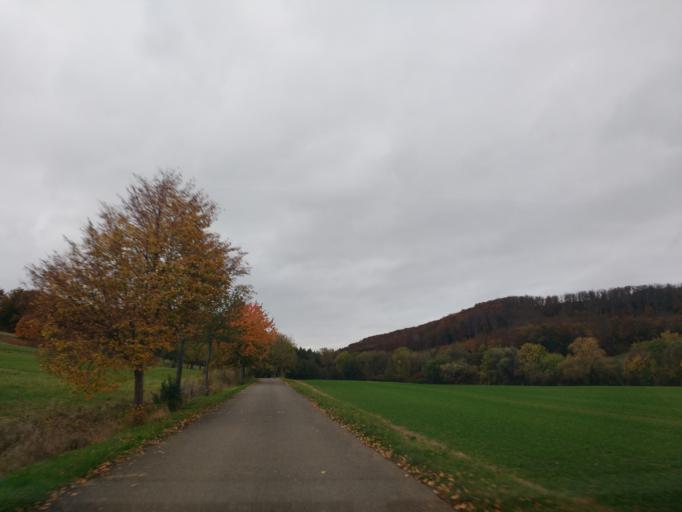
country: DE
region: Thuringia
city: Buhla
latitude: 51.4247
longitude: 10.4194
